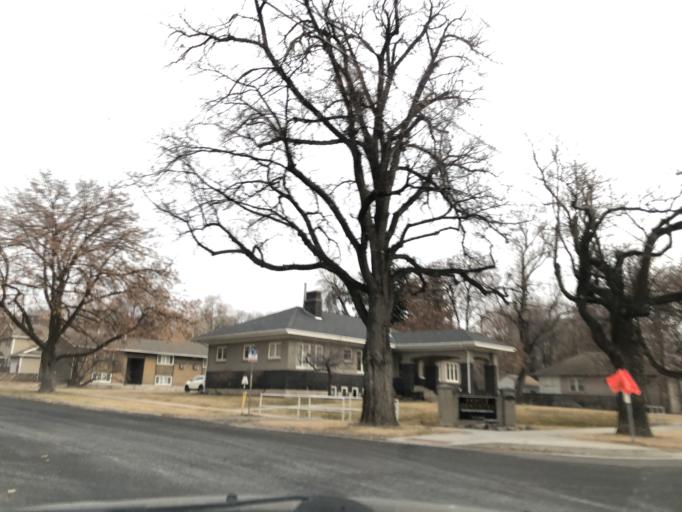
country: US
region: Utah
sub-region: Cache County
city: Logan
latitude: 41.7371
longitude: -111.8296
